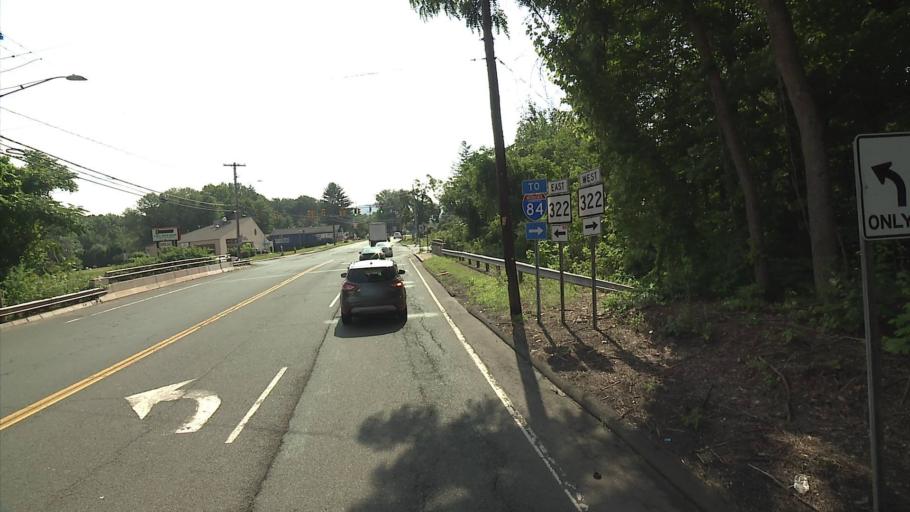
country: US
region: Connecticut
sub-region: New Haven County
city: Cheshire Village
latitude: 41.5648
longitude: -72.8906
